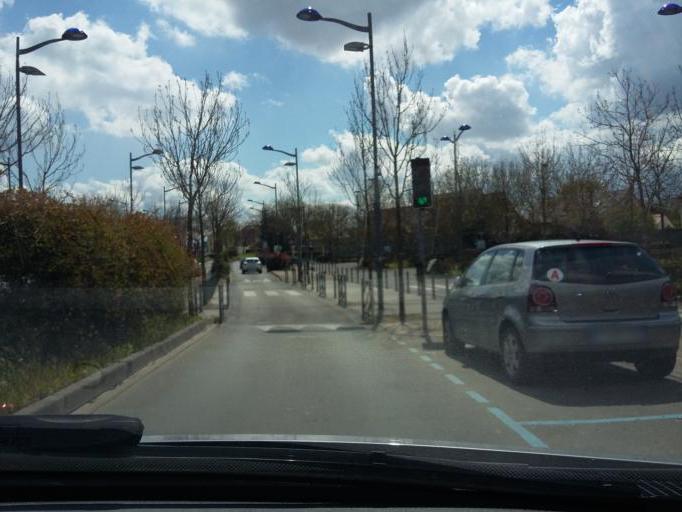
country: FR
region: Ile-de-France
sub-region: Departement du Val-d'Oise
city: Saint-Gratien
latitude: 48.9750
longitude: 2.2732
